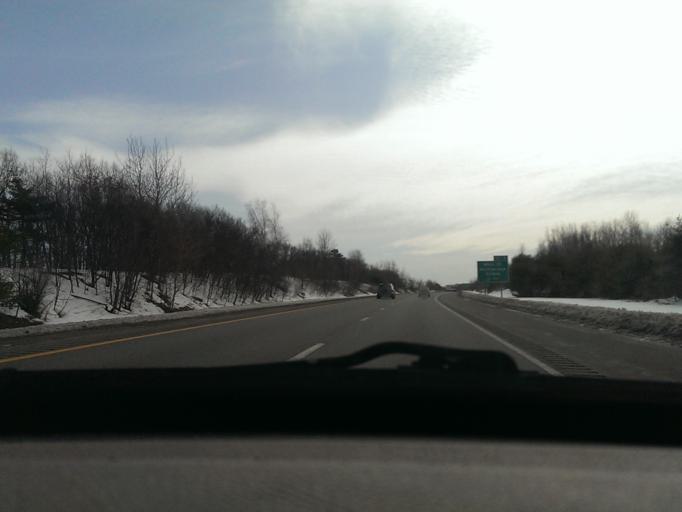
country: US
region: Massachusetts
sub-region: Worcester County
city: Whitinsville
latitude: 42.1136
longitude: -71.7054
